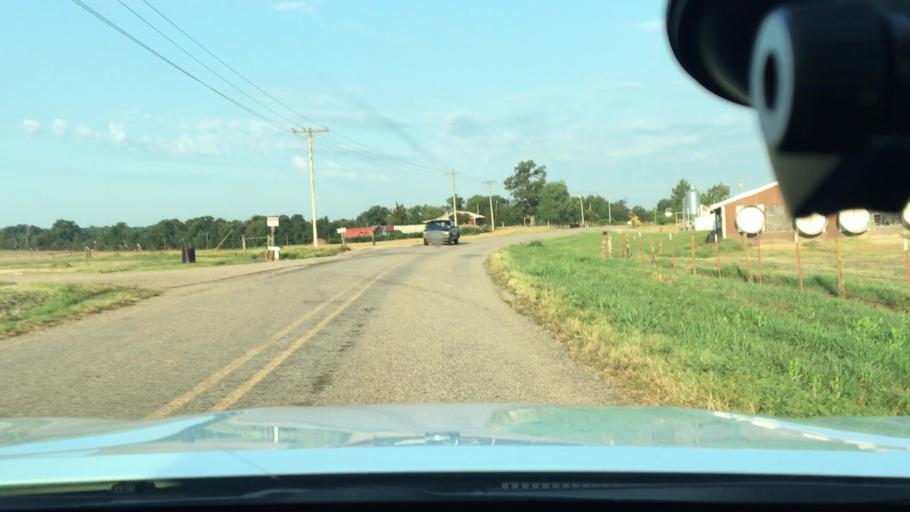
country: US
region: Arkansas
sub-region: Johnson County
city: Coal Hill
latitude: 35.3719
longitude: -93.5755
